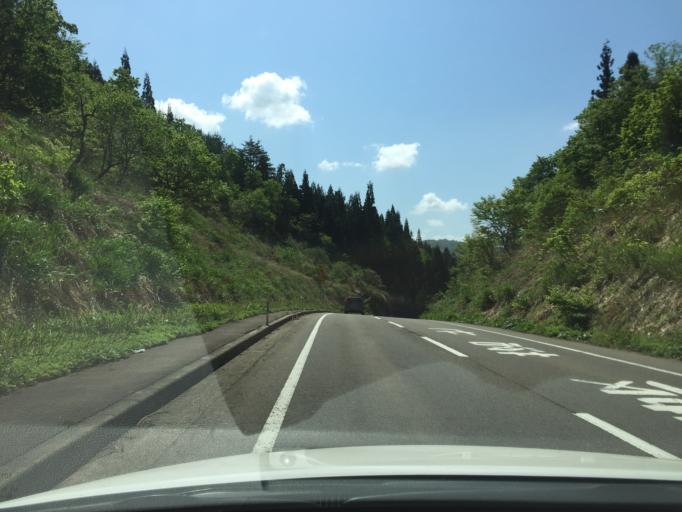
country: JP
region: Niigata
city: Kamo
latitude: 37.5838
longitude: 139.0924
